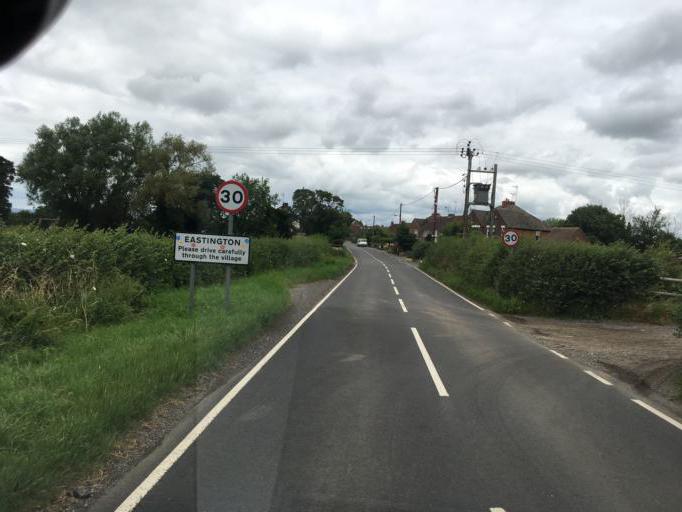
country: GB
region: England
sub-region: Gloucestershire
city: Stonehouse
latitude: 51.7384
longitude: -2.3207
